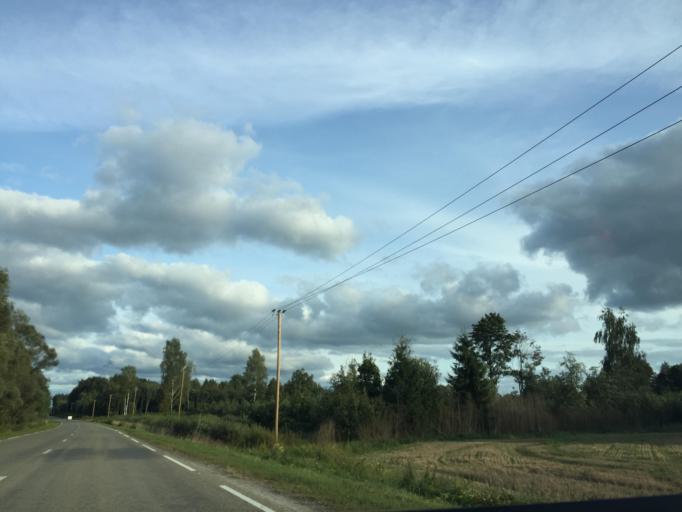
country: LV
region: Nereta
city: Nereta
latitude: 56.2898
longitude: 25.1246
